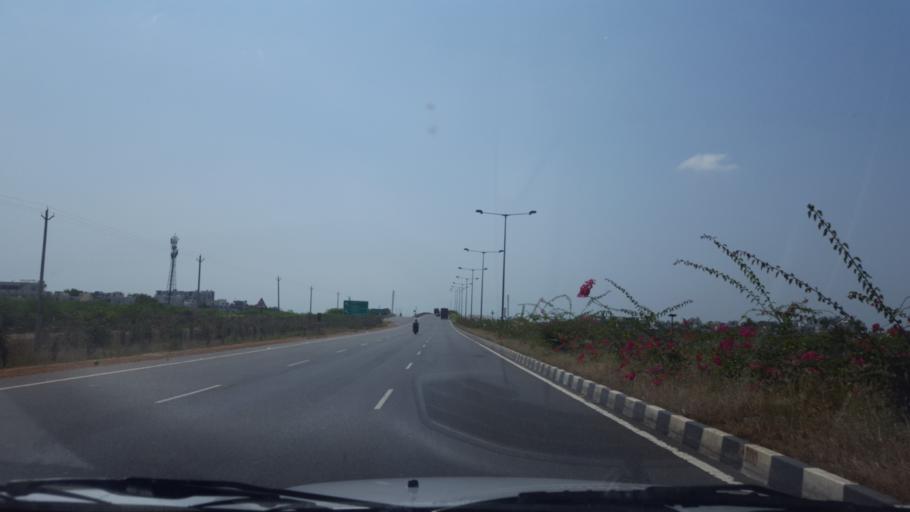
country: IN
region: Andhra Pradesh
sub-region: Prakasam
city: Ongole
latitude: 15.5020
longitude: 80.0706
